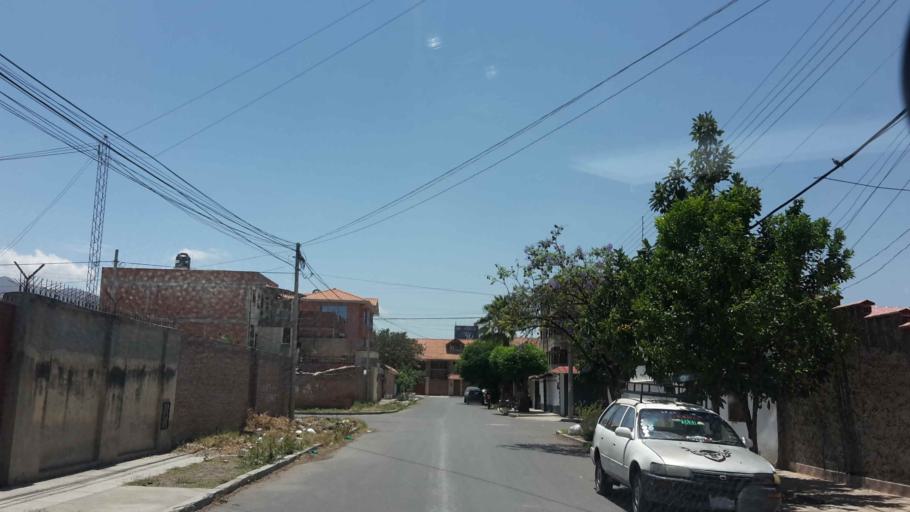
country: BO
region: Cochabamba
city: Cochabamba
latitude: -17.3772
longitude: -66.1938
